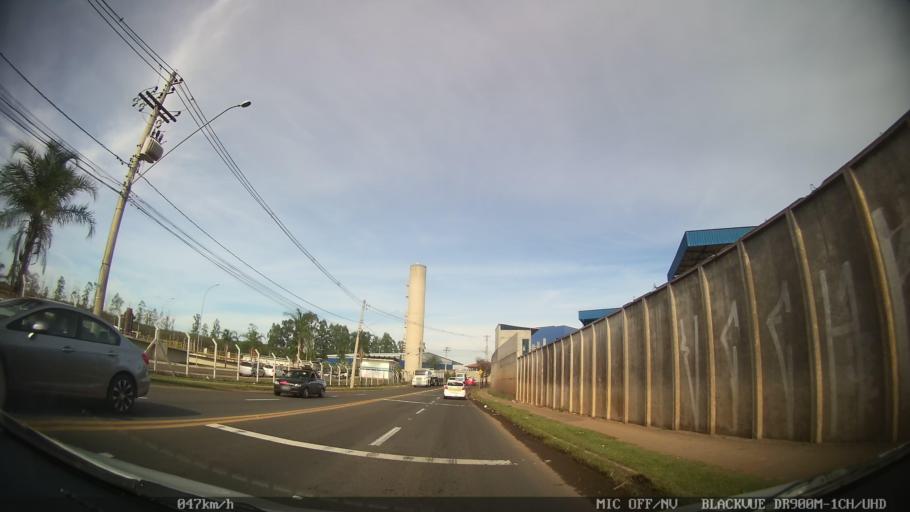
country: BR
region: Sao Paulo
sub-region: Piracicaba
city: Piracicaba
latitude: -22.6994
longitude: -47.6743
